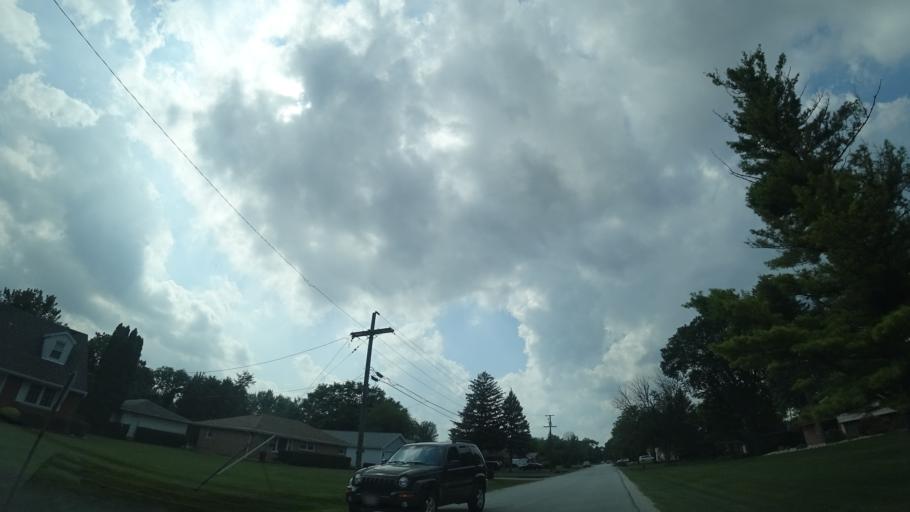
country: US
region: Illinois
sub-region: Cook County
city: Worth
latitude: 41.6798
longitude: -87.7833
